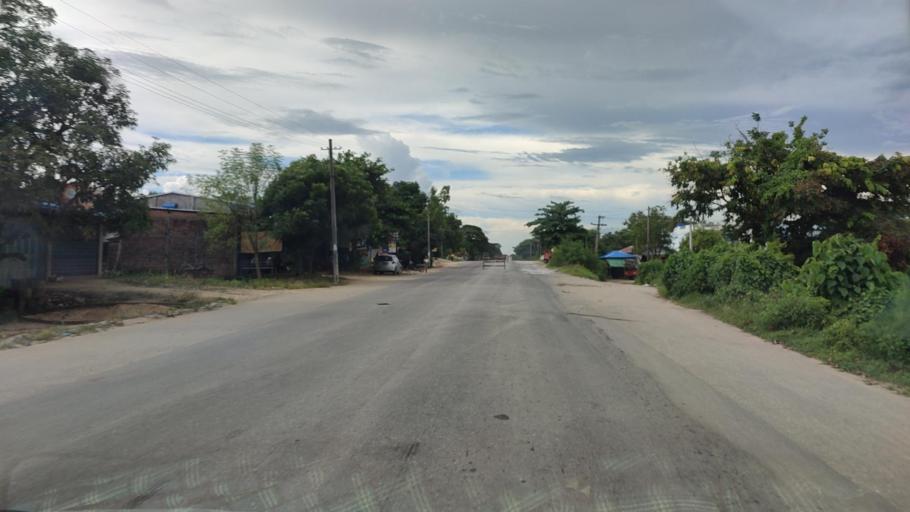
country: MM
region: Bago
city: Pyu
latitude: 18.5798
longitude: 96.4242
